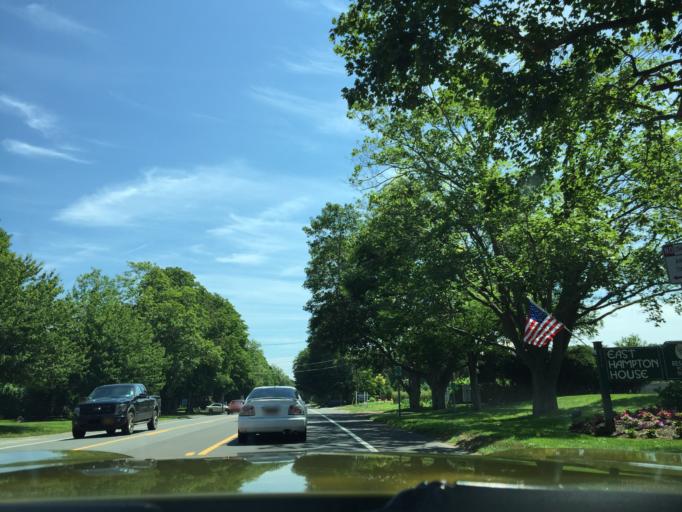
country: US
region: New York
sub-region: Suffolk County
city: East Hampton
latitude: 40.9678
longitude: -72.1690
